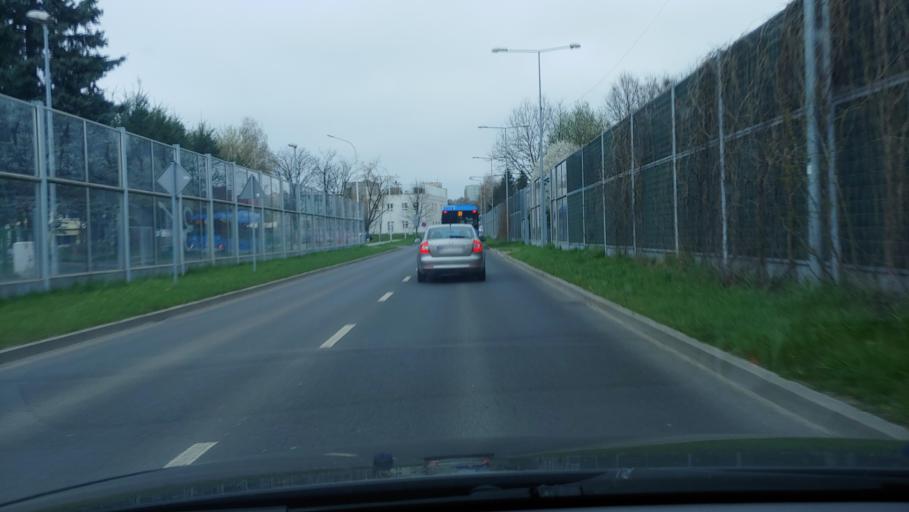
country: PL
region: Lesser Poland Voivodeship
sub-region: Powiat chrzanowski
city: Chrzanow
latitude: 50.1466
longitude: 19.4186
